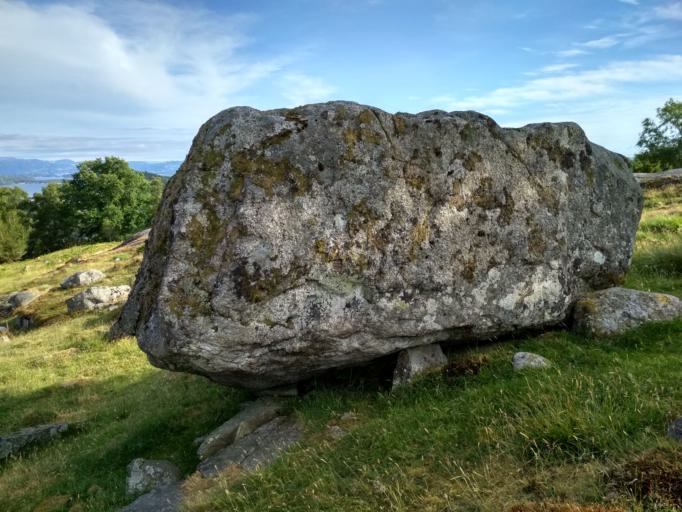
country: NO
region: Rogaland
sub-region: Finnoy
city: Judaberg
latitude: 59.2557
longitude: 5.8755
